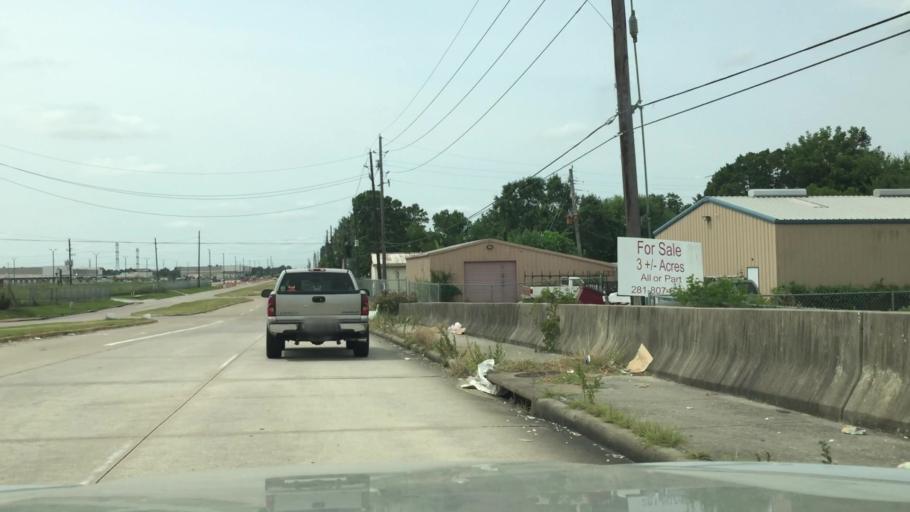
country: US
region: Texas
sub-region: Harris County
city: Jersey Village
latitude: 29.9485
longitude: -95.5470
